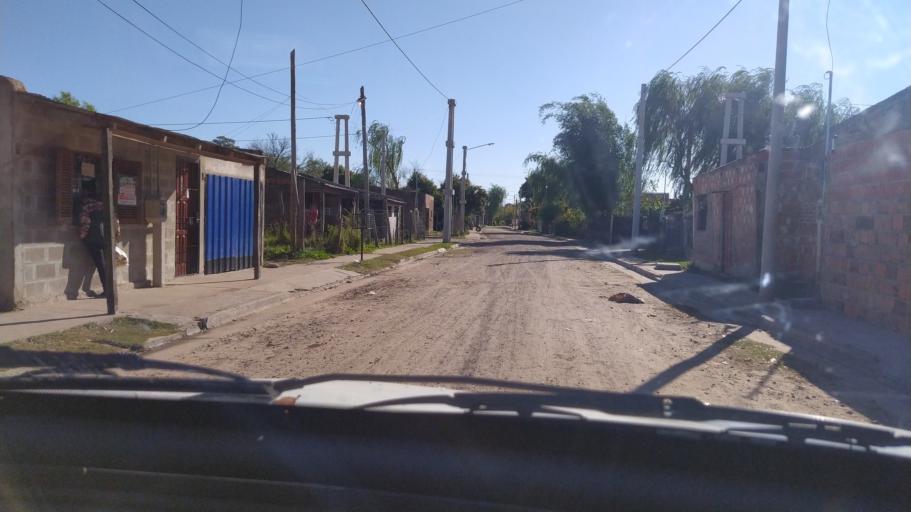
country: AR
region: Corrientes
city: Corrientes
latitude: -27.4996
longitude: -58.8060
